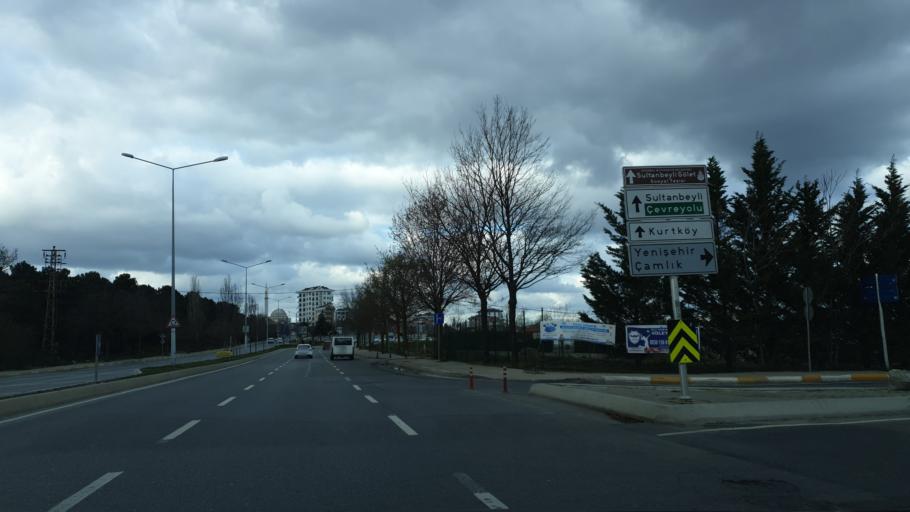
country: TR
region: Istanbul
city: Sultanbeyli
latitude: 40.9299
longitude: 29.2733
